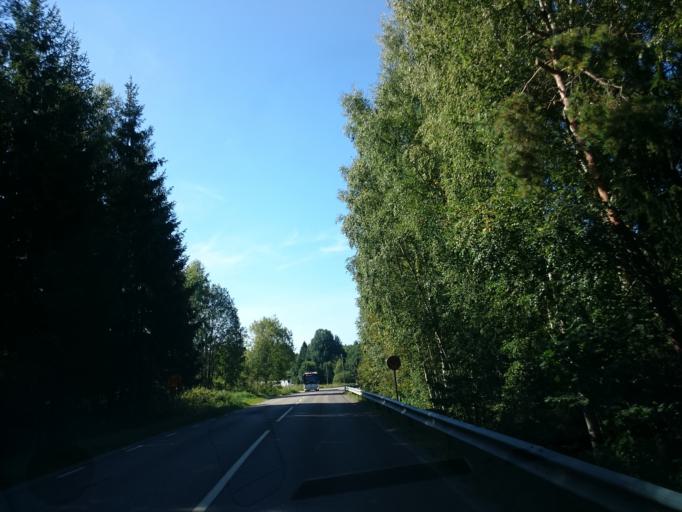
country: SE
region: OEstergoetland
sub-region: Norrkopings Kommun
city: Krokek
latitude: 58.6658
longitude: 16.4088
